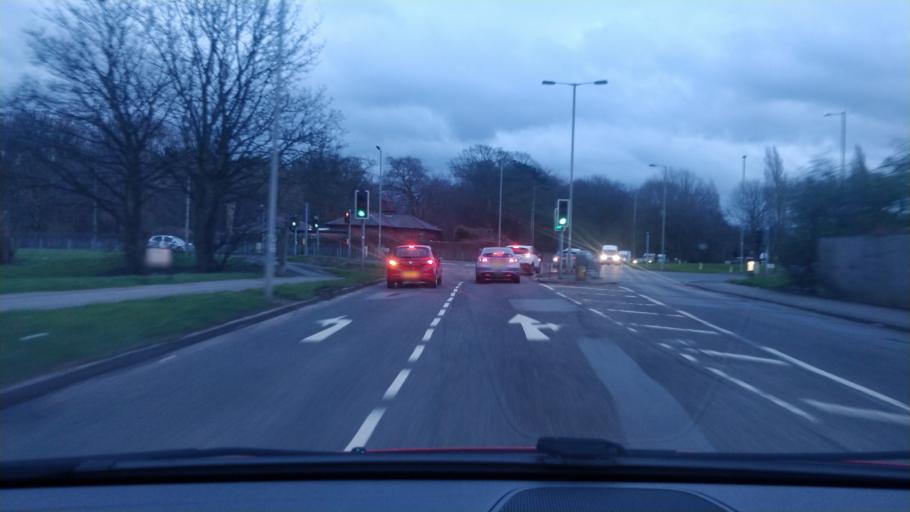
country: GB
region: England
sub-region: Knowsley
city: Kirkby
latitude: 53.4466
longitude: -2.9000
